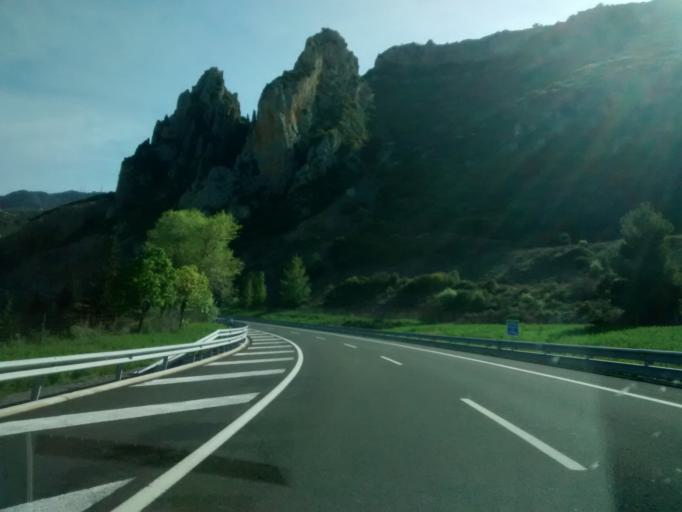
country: ES
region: Aragon
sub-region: Provincia de Huesca
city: Nueno
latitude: 42.2732
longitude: -0.4308
